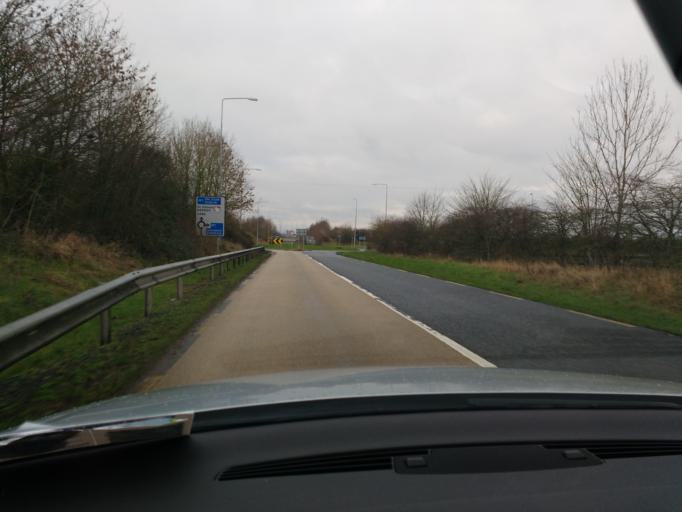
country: IE
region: Munster
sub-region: North Tipperary
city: Nenagh
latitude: 52.8474
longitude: -8.1550
